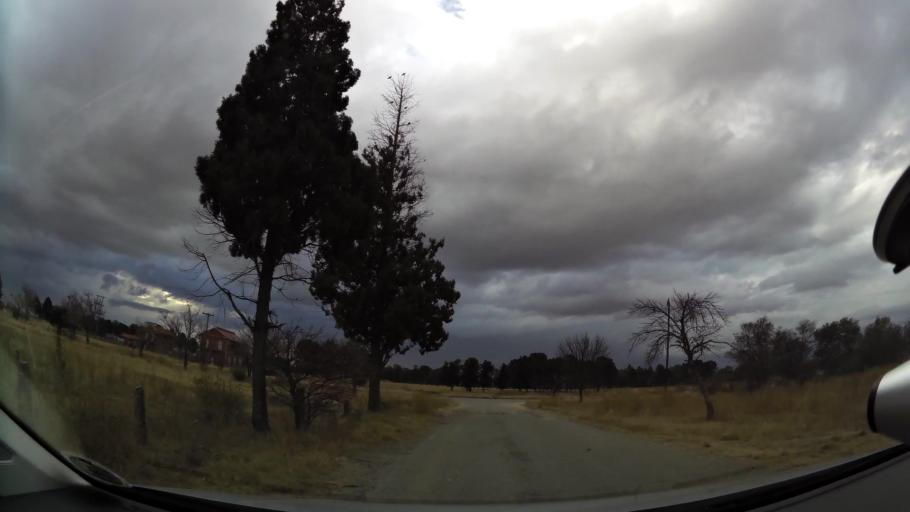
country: ZA
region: Orange Free State
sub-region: Lejweleputswa District Municipality
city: Welkom
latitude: -27.9677
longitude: 26.7011
